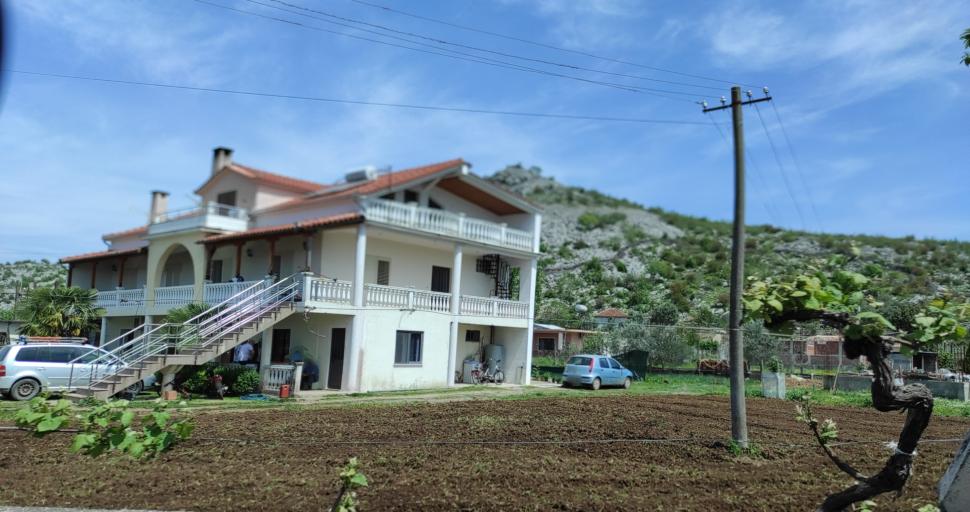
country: AL
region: Shkoder
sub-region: Rrethi i Malesia e Madhe
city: Gruemire
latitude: 42.1344
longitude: 19.5502
